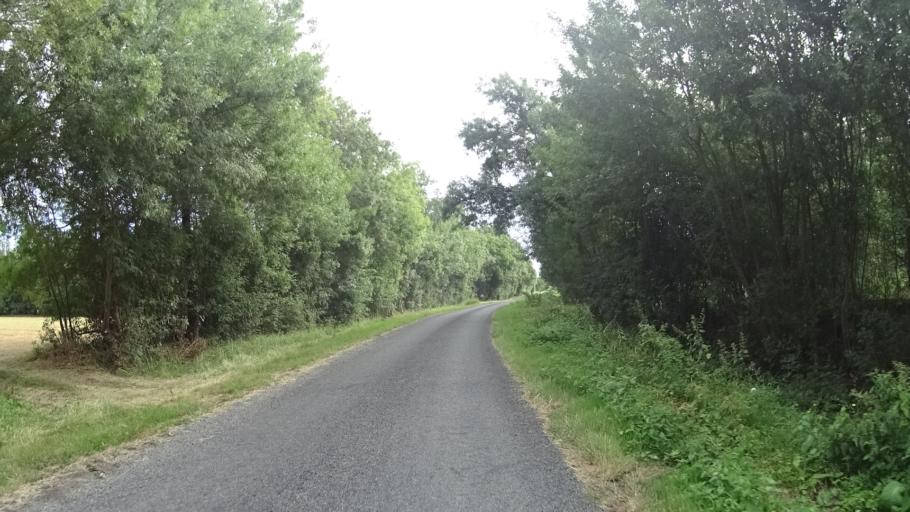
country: FR
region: Centre
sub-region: Departement d'Indre-et-Loire
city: Chouze-sur-Loire
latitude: 47.2044
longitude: 0.1063
